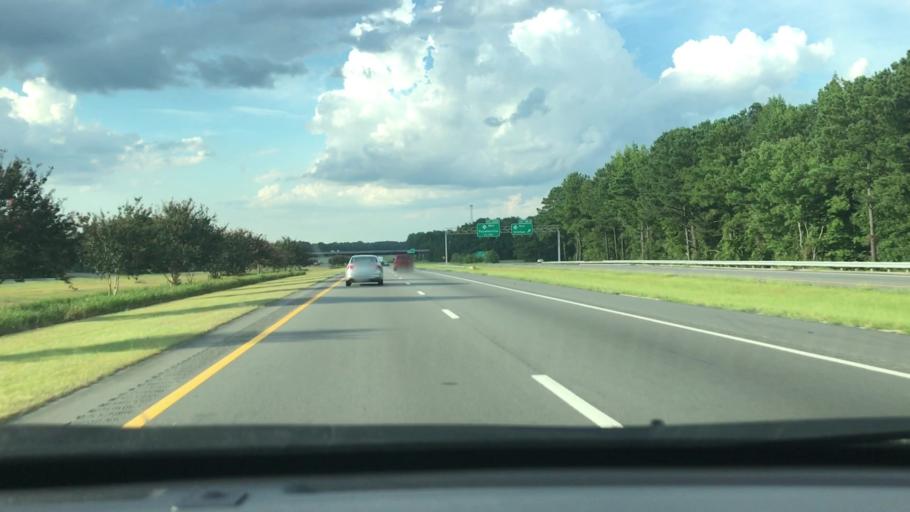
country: US
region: North Carolina
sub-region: Cumberland County
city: Vander
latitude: 35.0369
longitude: -78.8050
